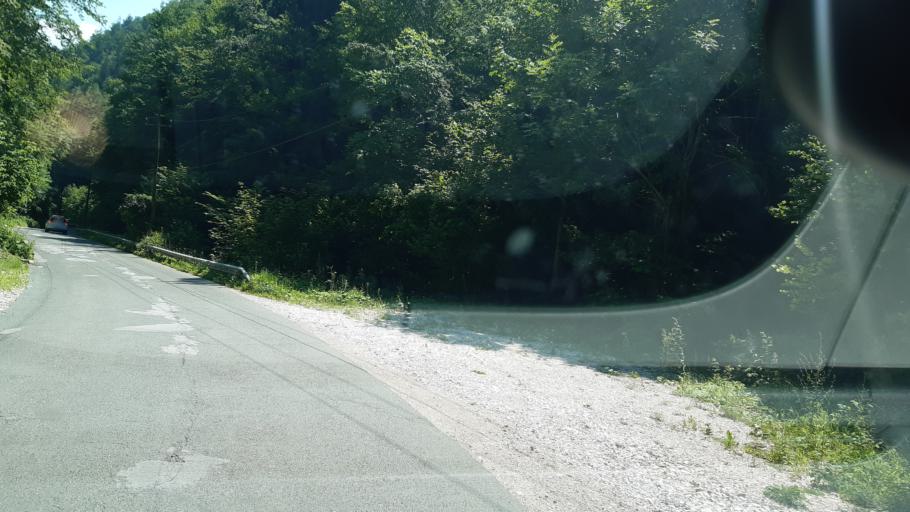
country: SI
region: Cerklje na Gorenjskem
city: Cerklje na Gorenjskem
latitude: 46.2831
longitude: 14.4946
